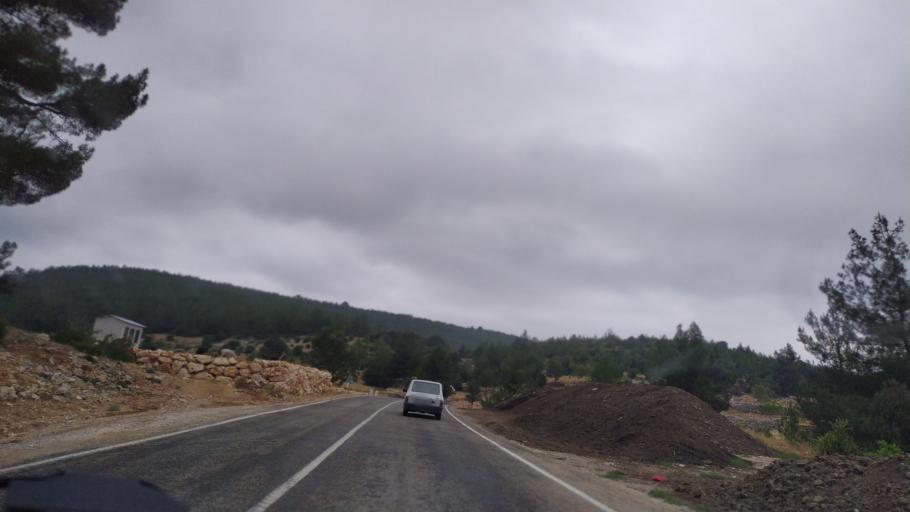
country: TR
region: Mersin
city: Silifke
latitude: 36.5408
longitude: 33.9367
